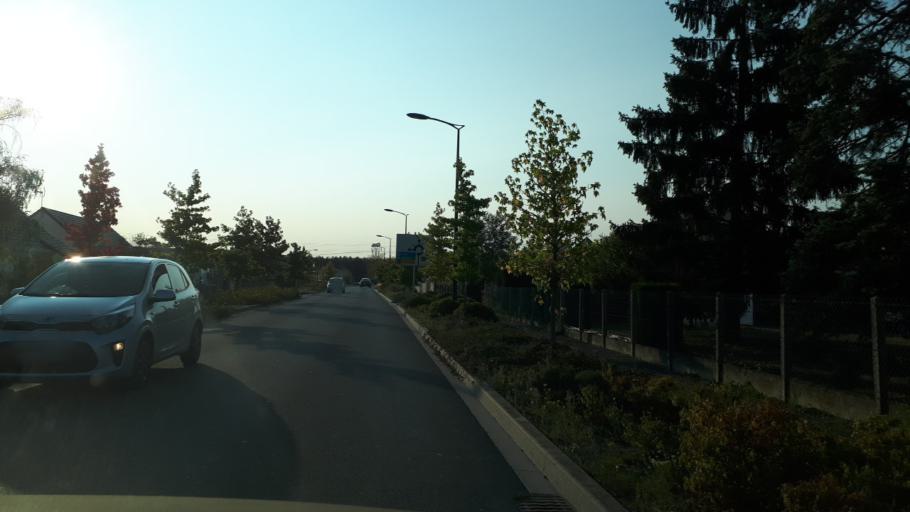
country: FR
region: Centre
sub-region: Departement du Loir-et-Cher
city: Romorantin-Lanthenay
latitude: 47.3675
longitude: 1.7158
